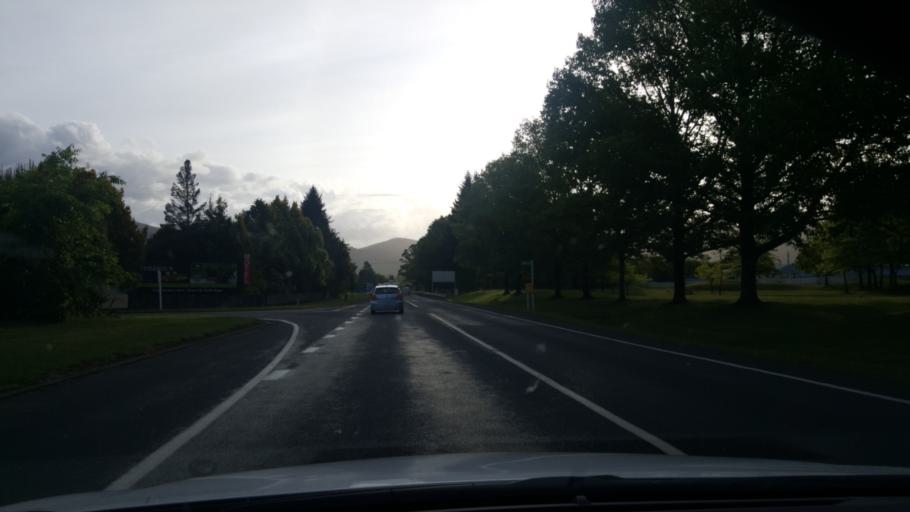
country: NZ
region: Waikato
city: Turangi
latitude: -38.9884
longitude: 175.8157
